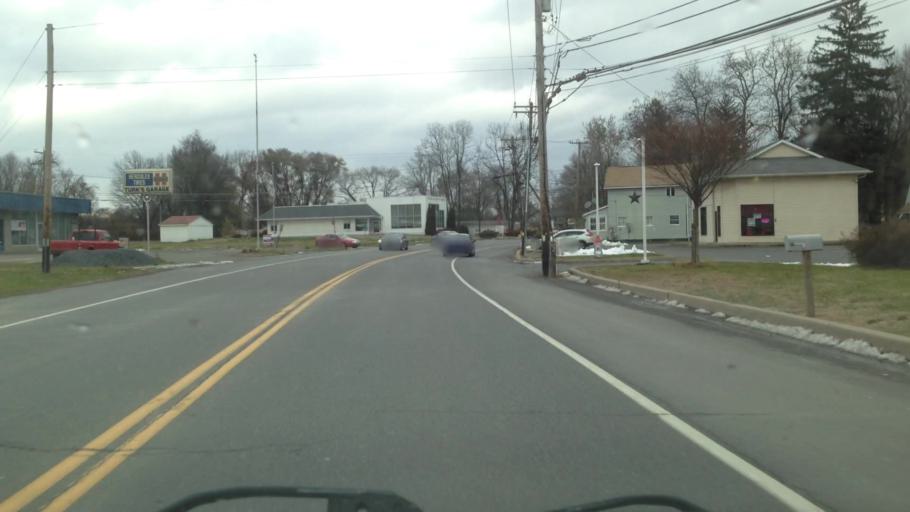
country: US
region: New York
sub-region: Ulster County
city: Saugerties South
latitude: 42.0544
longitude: -73.9563
